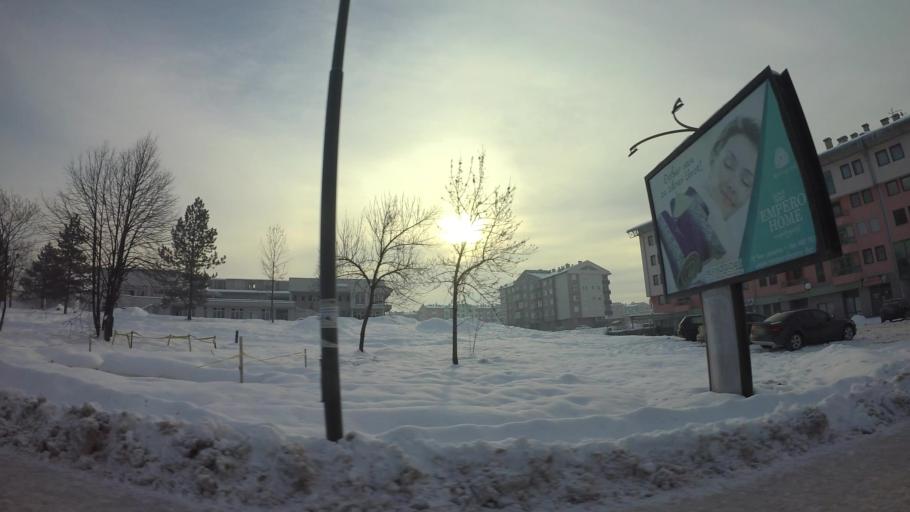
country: BA
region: Federation of Bosnia and Herzegovina
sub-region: Kanton Sarajevo
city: Sarajevo
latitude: 43.8227
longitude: 18.3613
